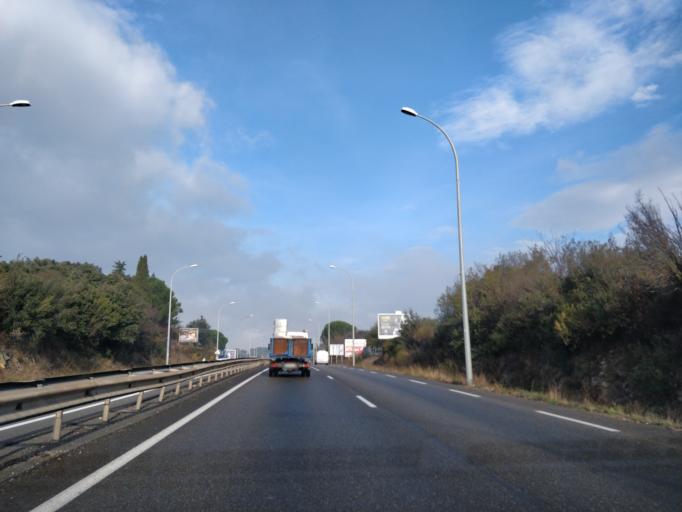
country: FR
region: Languedoc-Roussillon
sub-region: Departement du Gard
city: Nimes
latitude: 43.8364
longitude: 4.3210
